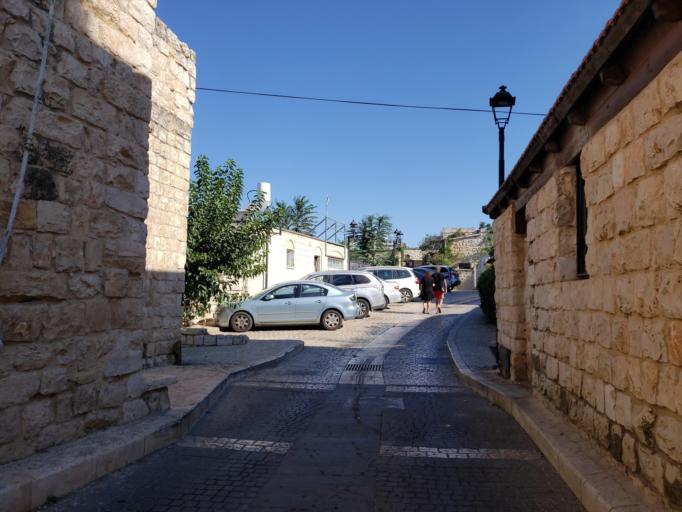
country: IL
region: Northern District
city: Safed
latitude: 32.9654
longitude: 35.4941
